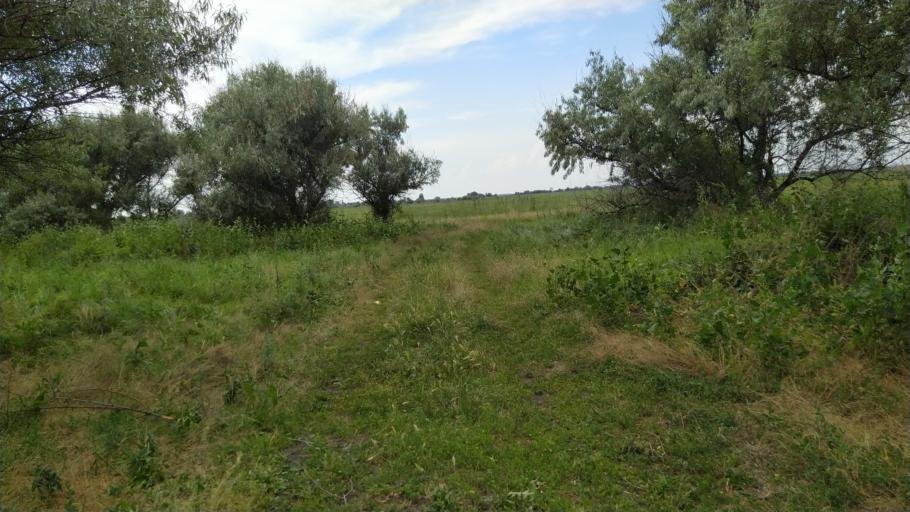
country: RU
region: Rostov
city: Kuleshovka
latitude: 47.1238
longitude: 39.6259
